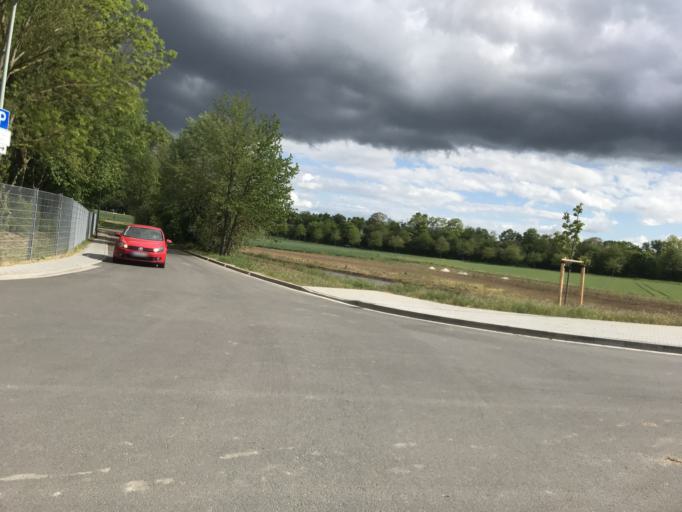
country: DE
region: Rheinland-Pfalz
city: Nieder-Olm
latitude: 49.9010
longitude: 8.1928
